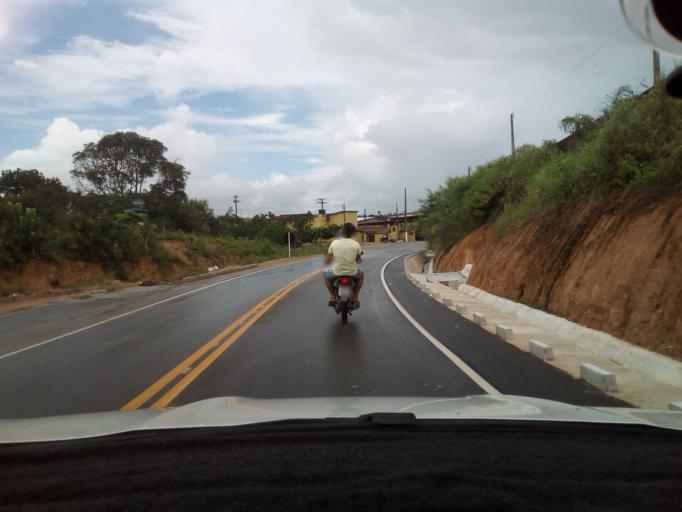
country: BR
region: Paraiba
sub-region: Pedras De Fogo
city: Pedras de Fogo
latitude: -7.4008
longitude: -35.1271
